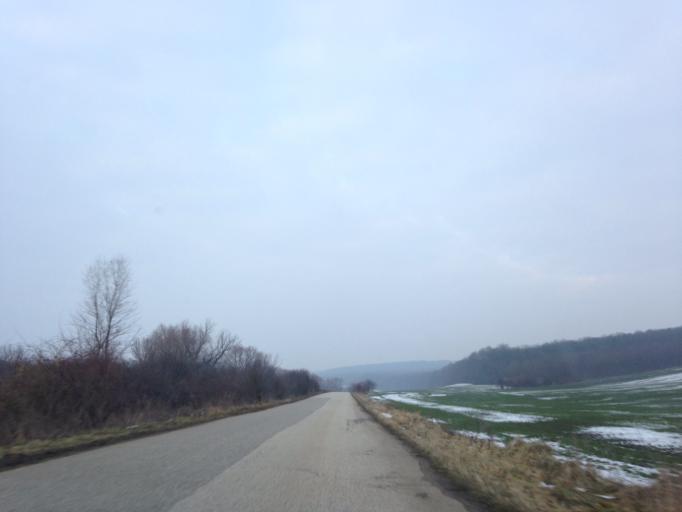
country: SK
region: Nitriansky
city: Surany
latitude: 48.0491
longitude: 18.3690
